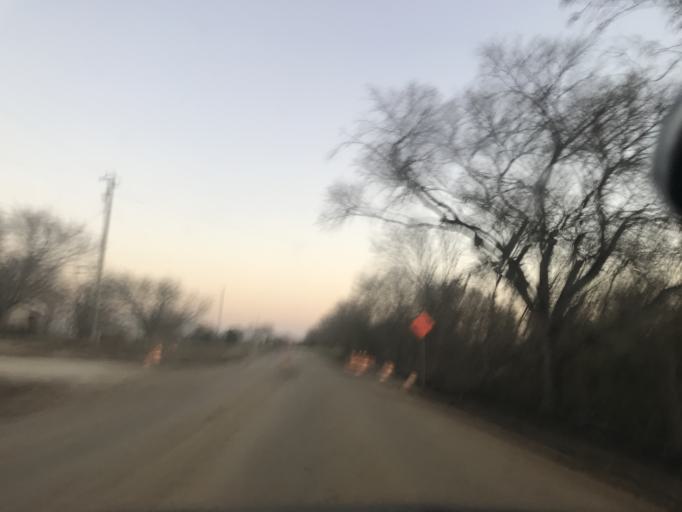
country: US
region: Texas
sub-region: Williamson County
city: Hutto
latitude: 30.5054
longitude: -97.5203
